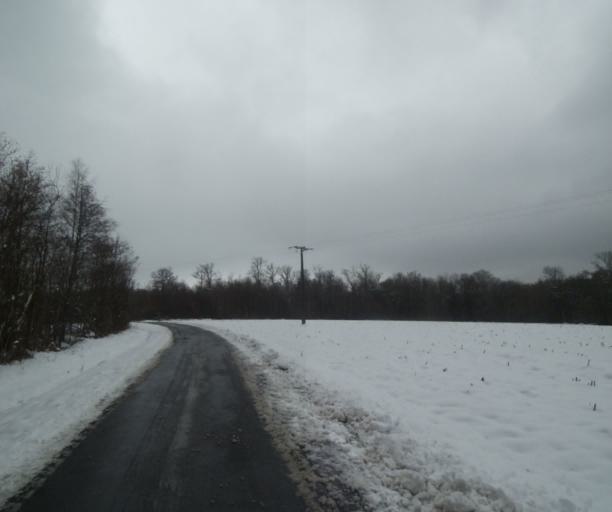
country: FR
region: Champagne-Ardenne
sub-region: Departement de la Haute-Marne
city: Laneuville-a-Remy
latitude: 48.4684
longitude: 4.8948
